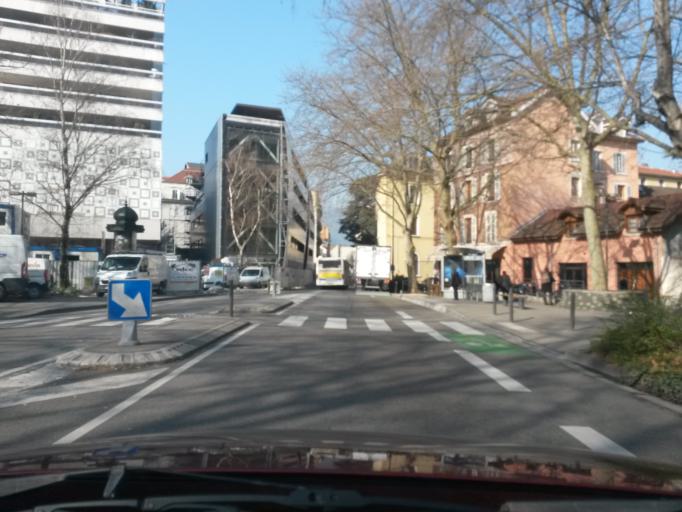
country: FR
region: Rhone-Alpes
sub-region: Departement de l'Isere
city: La Tronche
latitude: 45.1888
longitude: 5.7367
